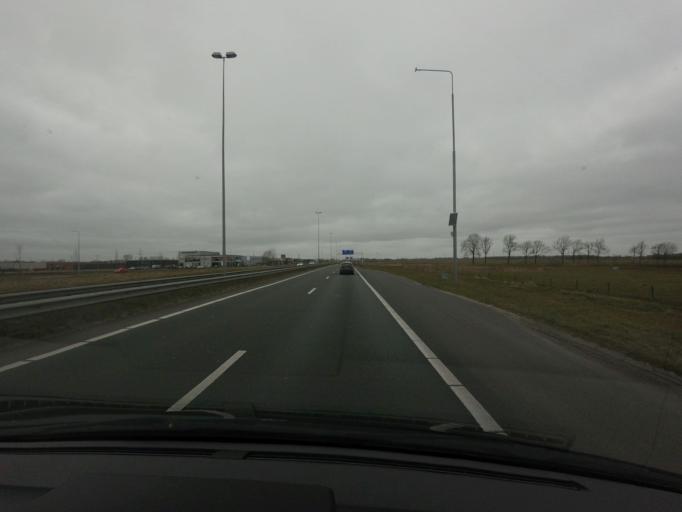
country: NL
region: Groningen
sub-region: Gemeente Haren
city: Haren
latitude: 53.2088
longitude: 6.6272
